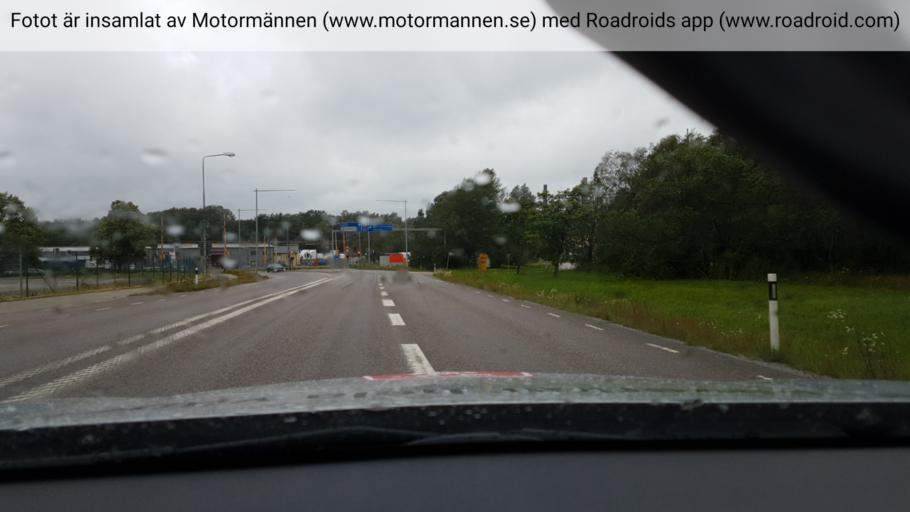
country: SE
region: Vaestra Goetaland
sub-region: Stenungsunds Kommun
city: Stenungsund
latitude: 58.0781
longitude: 11.8319
